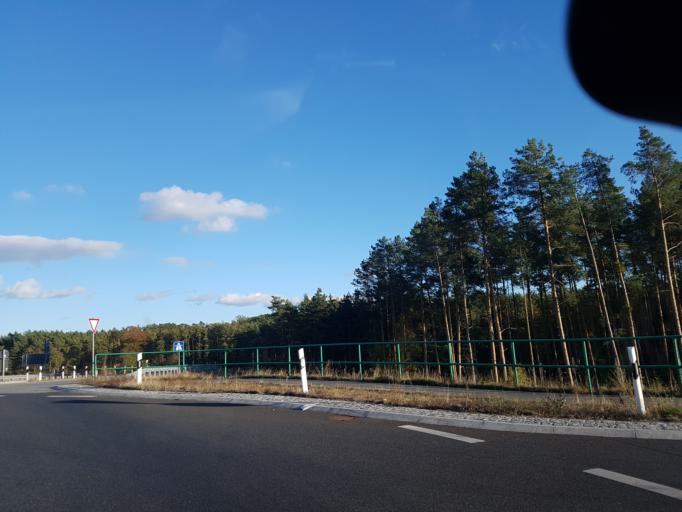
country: DE
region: Brandenburg
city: Kremmen
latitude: 52.7161
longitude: 12.9770
